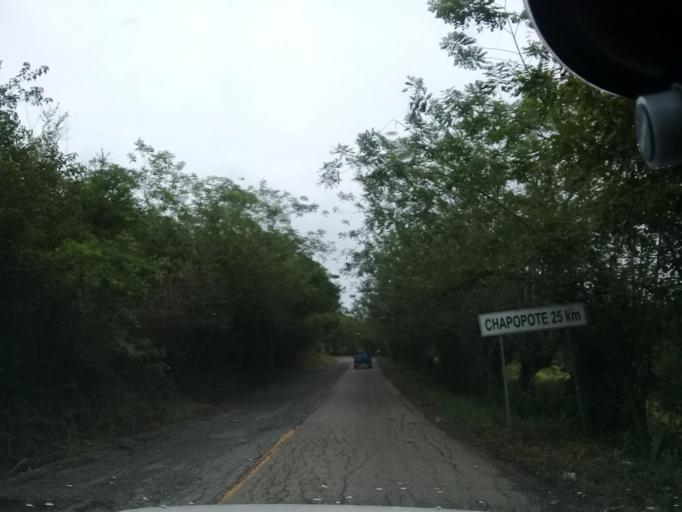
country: MX
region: Veracruz
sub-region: Chalma
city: San Pedro Coyutla
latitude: 21.2087
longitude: -98.3873
